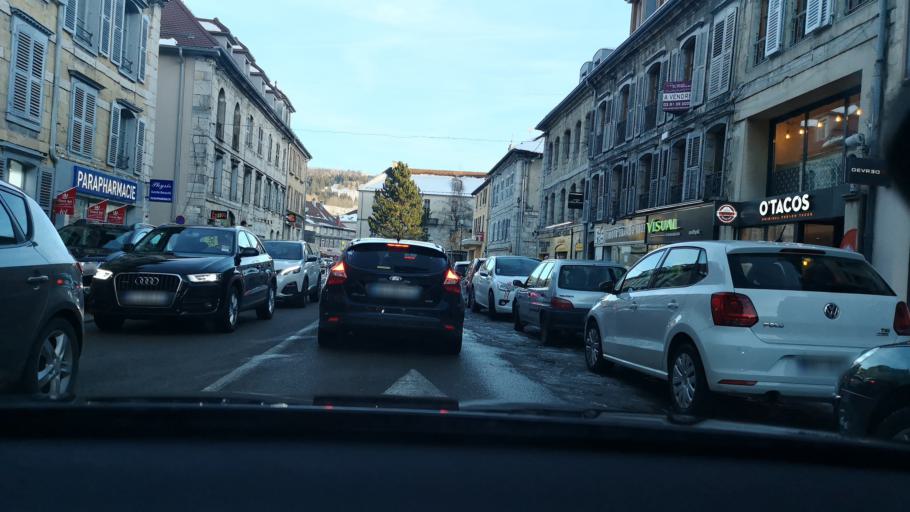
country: FR
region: Franche-Comte
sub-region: Departement du Doubs
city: Pontarlier
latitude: 46.9025
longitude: 6.3577
